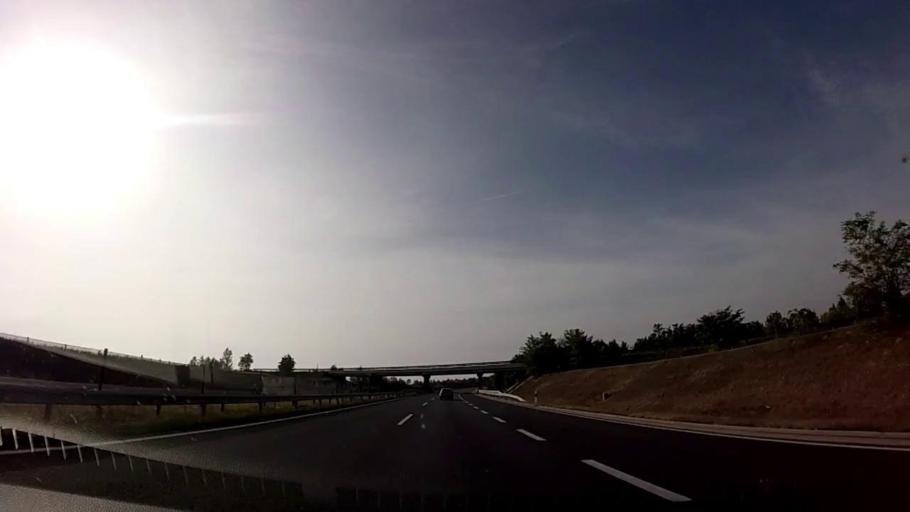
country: HU
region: Somogy
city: Zamardi
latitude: 46.8593
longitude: 17.9647
